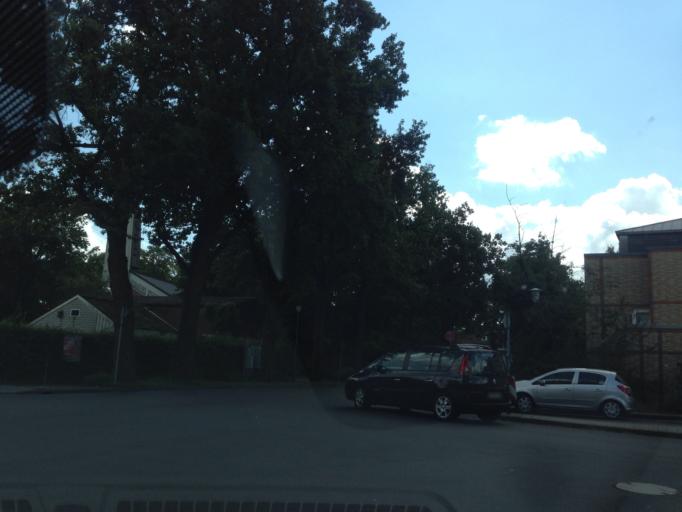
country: DE
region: North Rhine-Westphalia
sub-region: Regierungsbezirk Munster
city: Muenster
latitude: 51.9332
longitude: 7.6156
